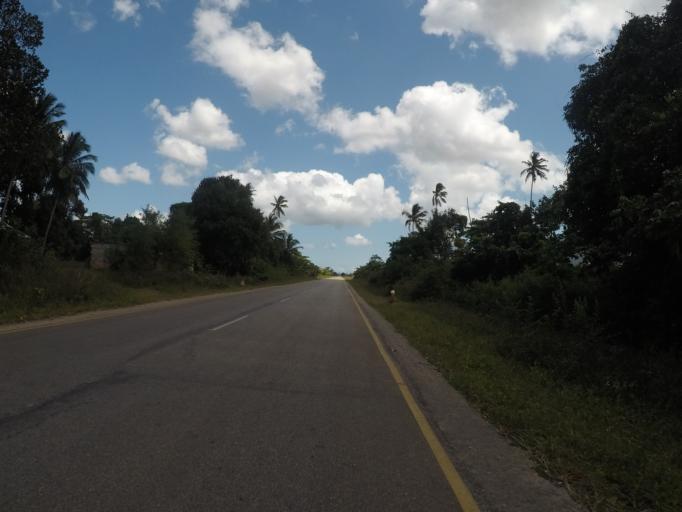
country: TZ
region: Zanzibar Central/South
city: Koani
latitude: -6.1831
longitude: 39.3719
